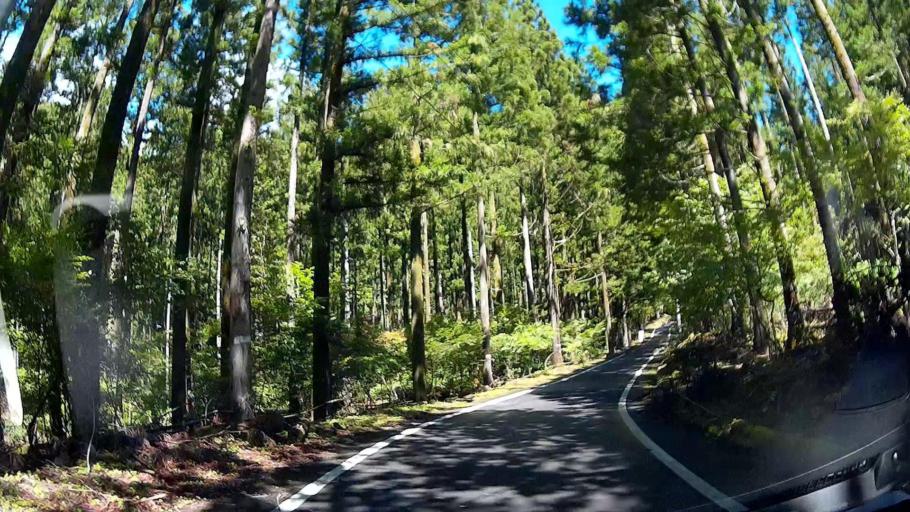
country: JP
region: Shizuoka
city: Fujinomiya
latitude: 35.2956
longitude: 138.3137
